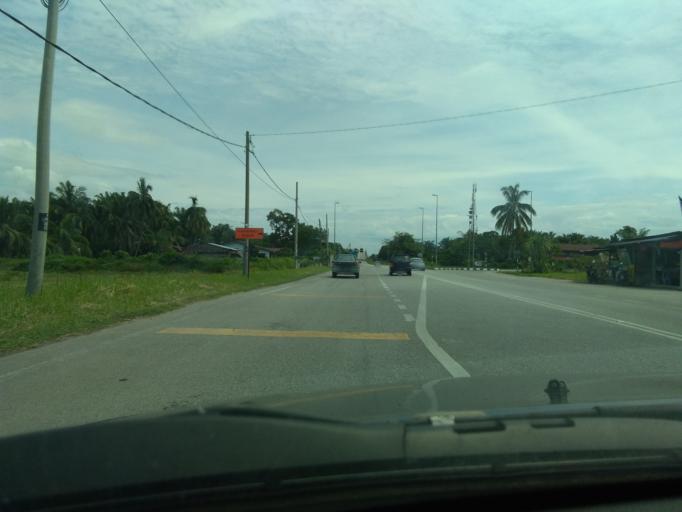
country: MY
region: Perak
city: Bagan Serai
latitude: 5.0597
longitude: 100.5942
